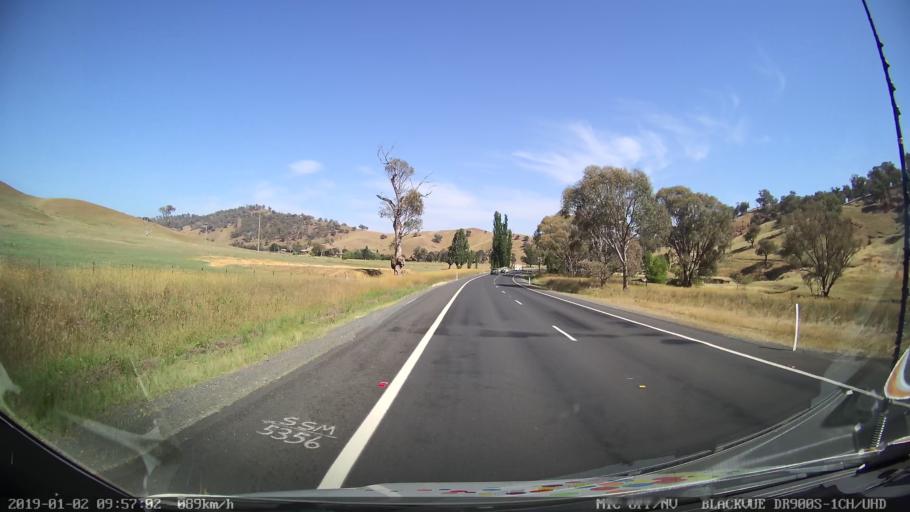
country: AU
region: New South Wales
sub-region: Tumut Shire
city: Tumut
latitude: -35.2100
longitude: 148.1696
